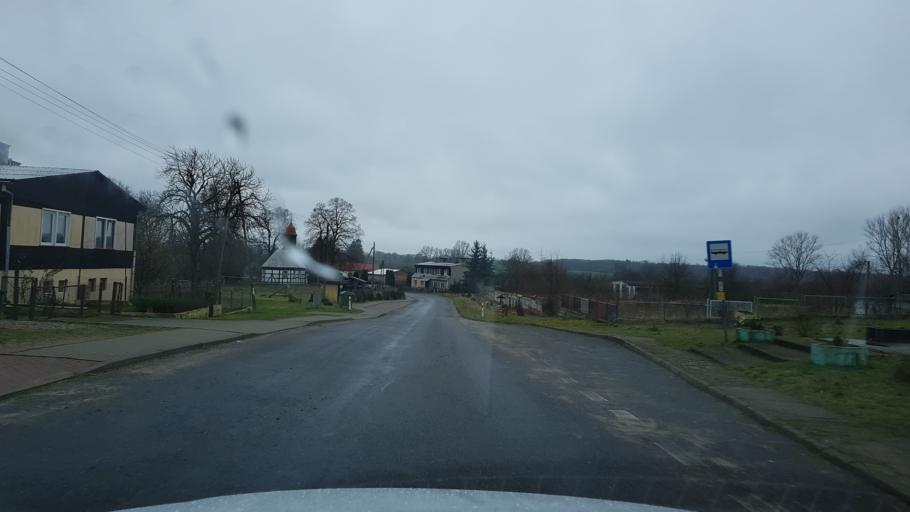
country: PL
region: West Pomeranian Voivodeship
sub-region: Powiat lobeski
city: Radowo Male
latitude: 53.6239
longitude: 15.4947
